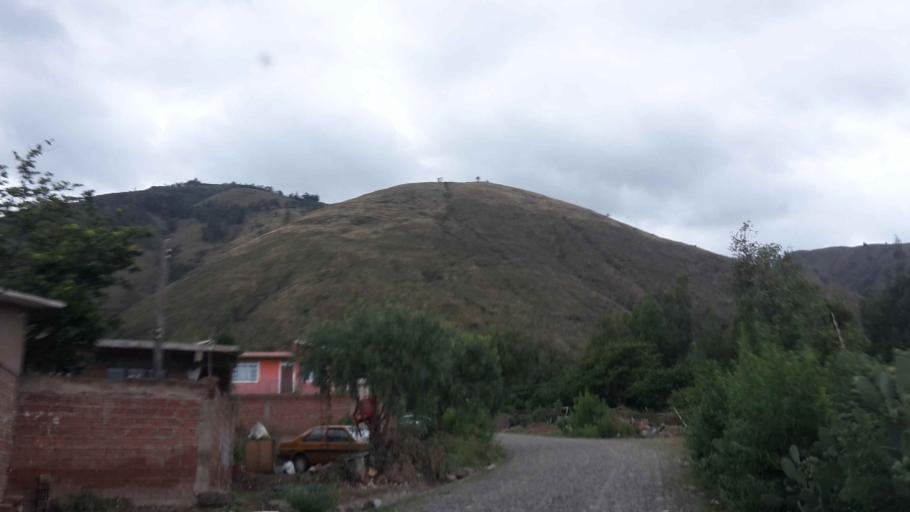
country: BO
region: Cochabamba
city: Cochabamba
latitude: -17.3750
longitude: -66.0563
